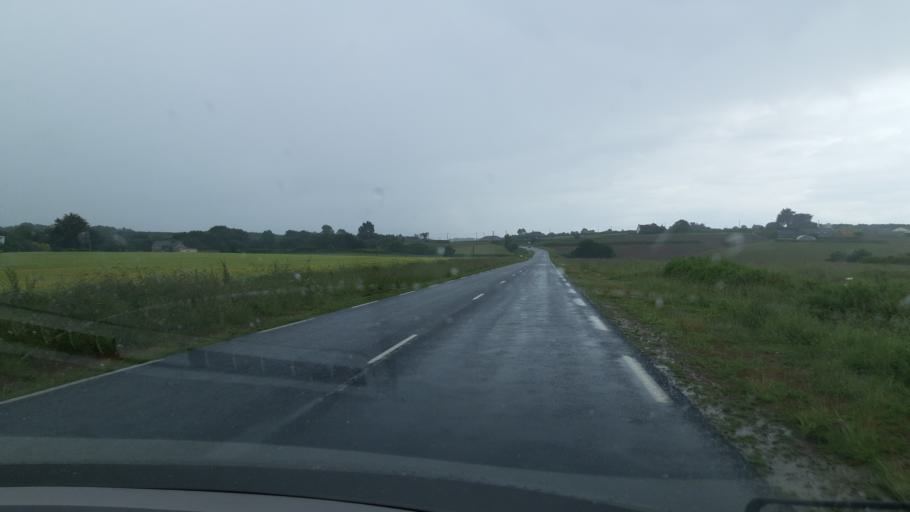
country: FR
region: Brittany
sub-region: Departement du Finistere
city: Plouvorn
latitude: 48.6110
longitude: -4.0568
